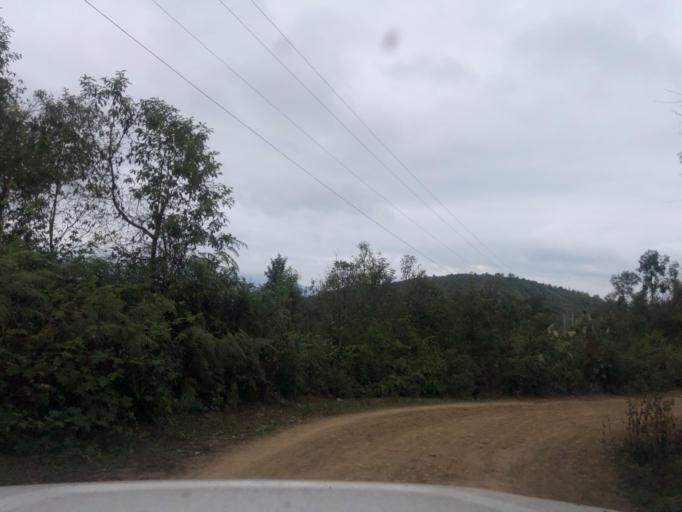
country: LA
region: Phongsali
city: Khoa
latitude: 21.2564
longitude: 102.5898
